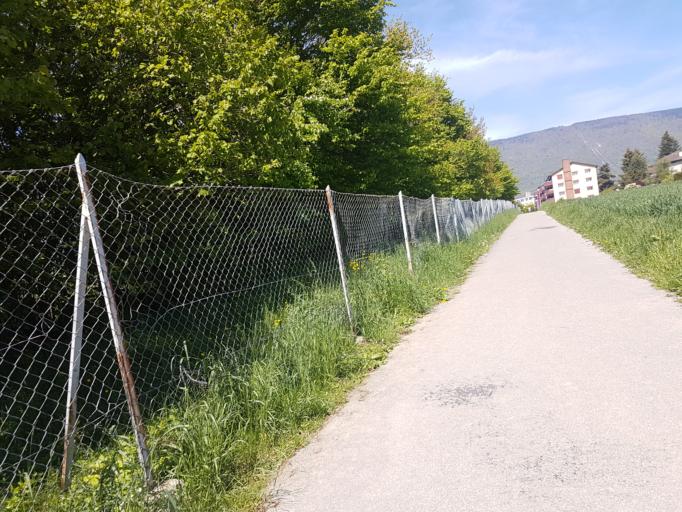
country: CH
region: Neuchatel
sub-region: Neuchatel District
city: Saint-Blaise
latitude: 47.0068
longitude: 7.0112
